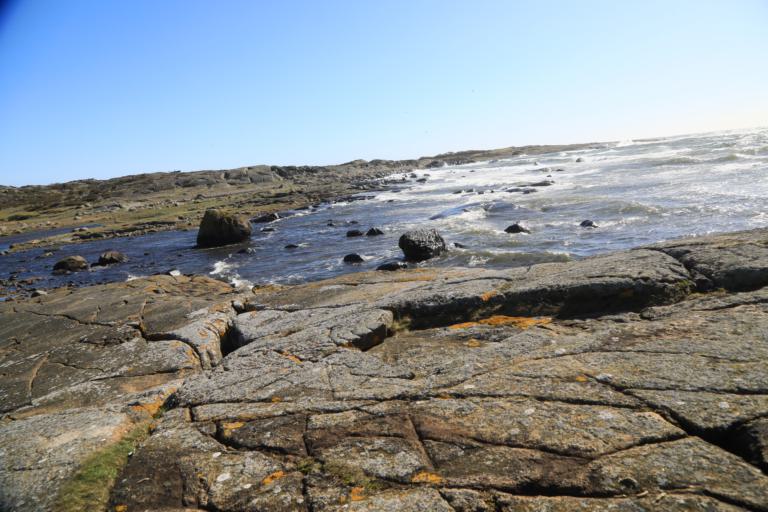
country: SE
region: Halland
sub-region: Varbergs Kommun
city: Varberg
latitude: 57.1203
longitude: 12.1917
